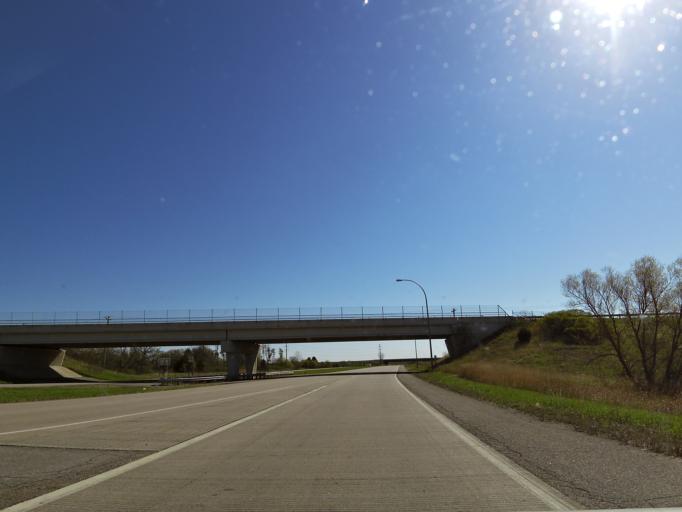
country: US
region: Minnesota
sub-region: Scott County
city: Prior Lake
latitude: 44.7839
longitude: -93.4098
